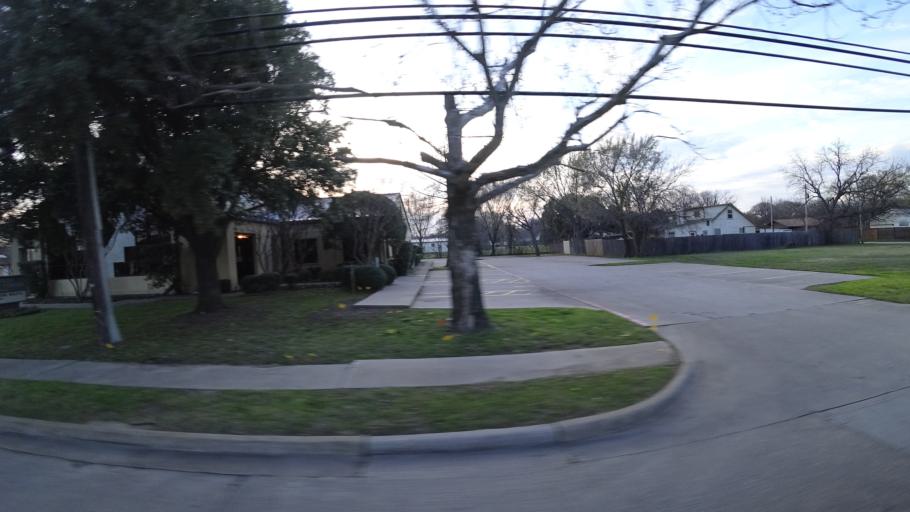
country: US
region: Texas
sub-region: Denton County
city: Lewisville
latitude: 33.0473
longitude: -97.0015
